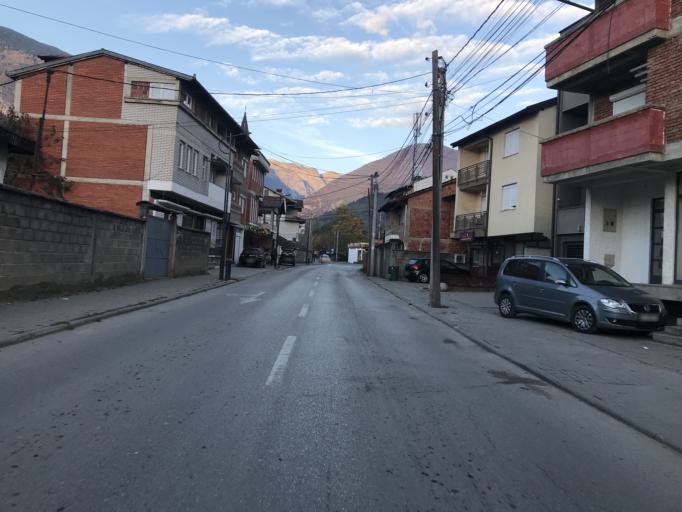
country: XK
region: Pec
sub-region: Komuna e Pejes
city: Peje
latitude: 42.6613
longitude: 20.2798
